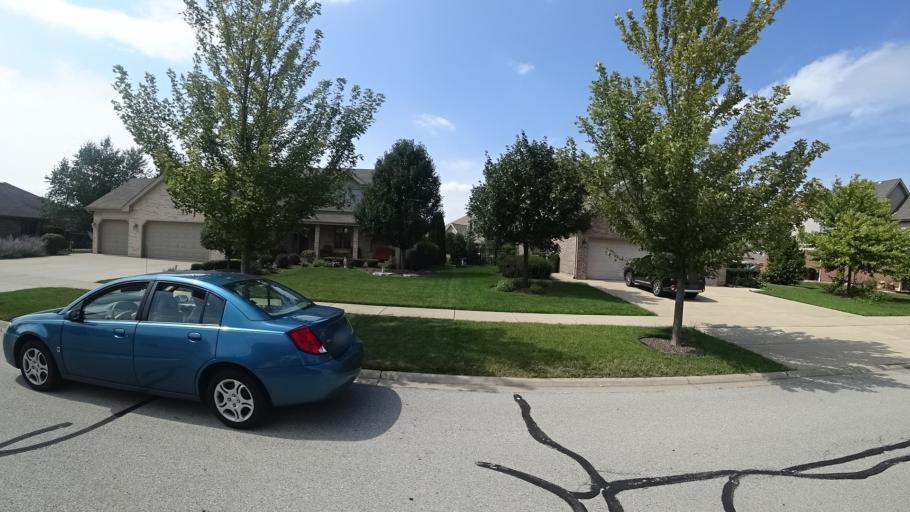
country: US
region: Illinois
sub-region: Cook County
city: Orland Hills
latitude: 41.5688
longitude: -87.8246
